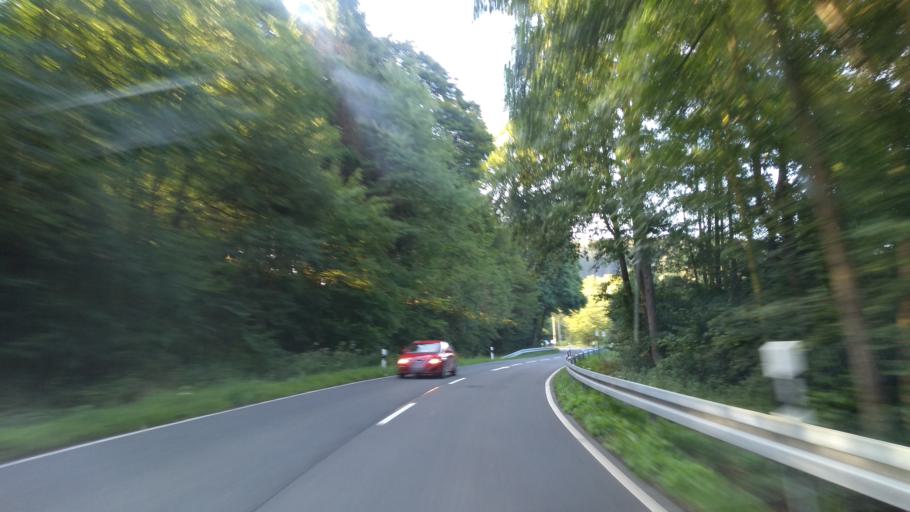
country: DE
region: North Rhine-Westphalia
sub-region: Regierungsbezirk Koln
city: Gummersbach
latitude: 51.0149
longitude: 7.5390
